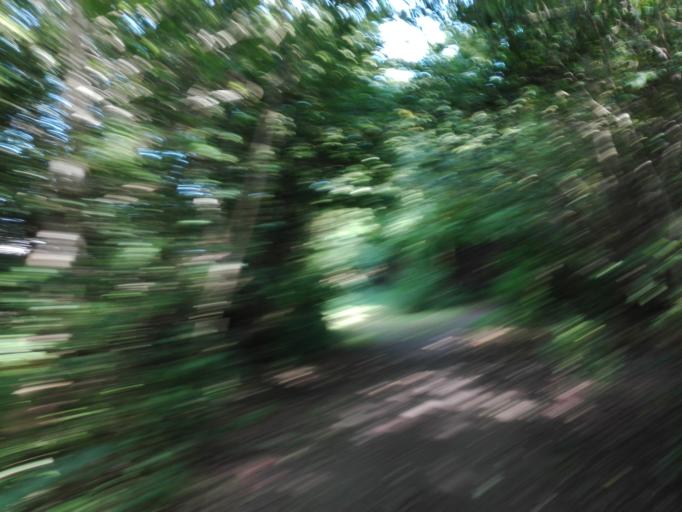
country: DK
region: Central Jutland
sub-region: Arhus Kommune
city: Marslet
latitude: 56.0874
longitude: 10.1508
